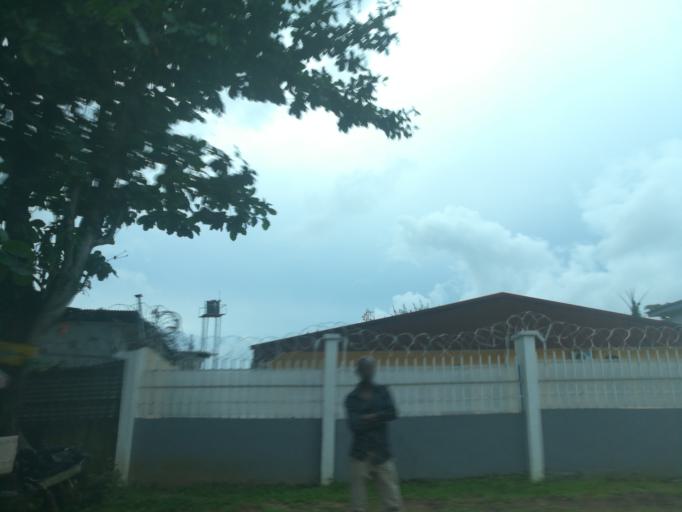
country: NG
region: Rivers
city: Port Harcourt
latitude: 4.8189
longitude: 6.9994
